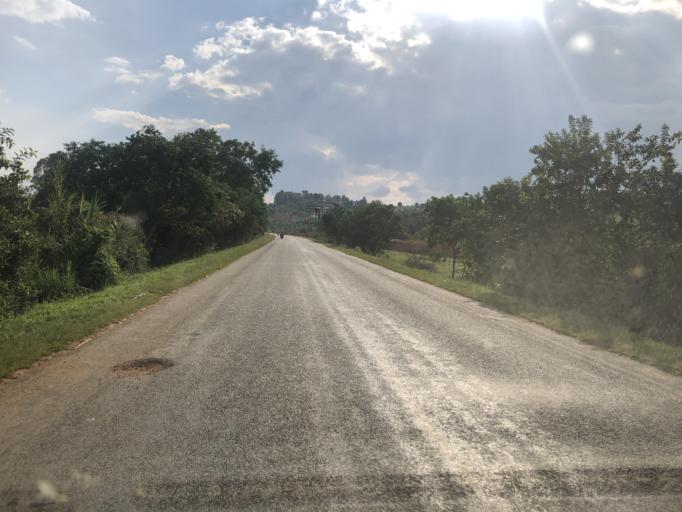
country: UG
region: Western Region
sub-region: Bushenyi District
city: Bushenyi
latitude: -0.5433
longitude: 30.2118
